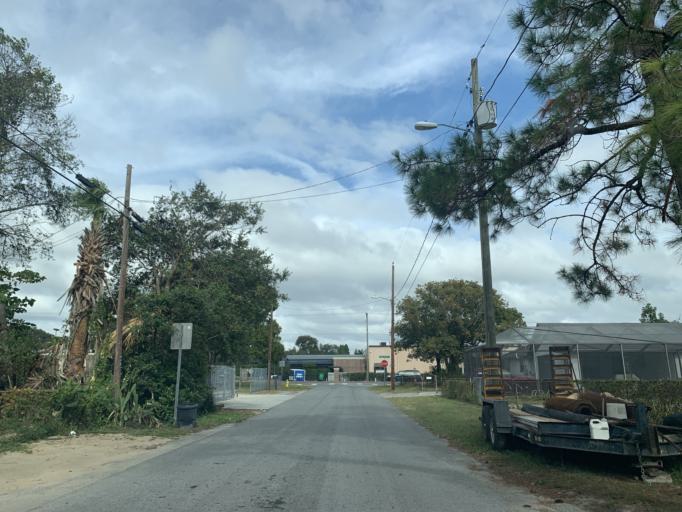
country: US
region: Florida
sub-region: Hillsborough County
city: East Lake-Orient Park
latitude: 27.9808
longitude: -82.3994
